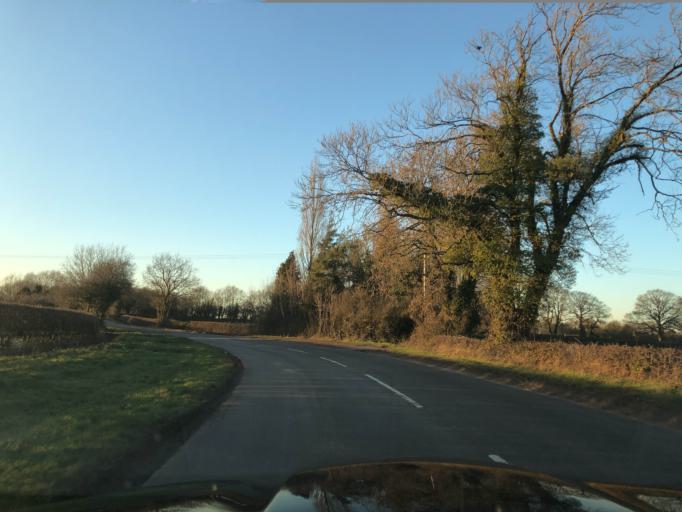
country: GB
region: England
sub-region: Warwickshire
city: Harbury
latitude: 52.2207
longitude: -1.4464
